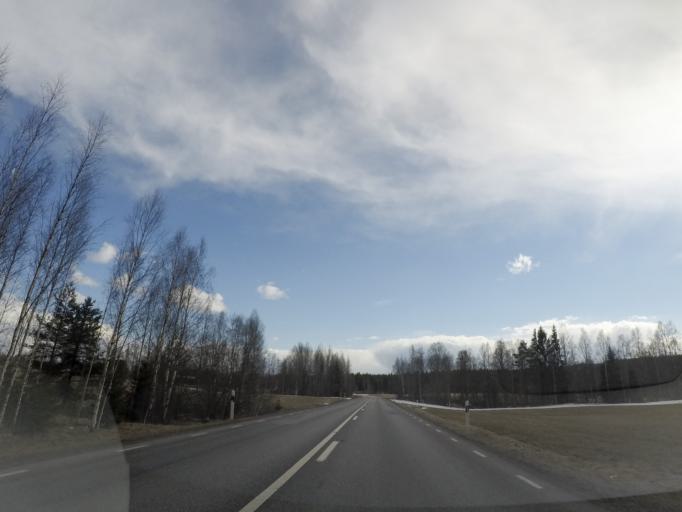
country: SE
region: Vaestmanland
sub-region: Skinnskattebergs Kommun
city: Skinnskatteberg
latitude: 59.8695
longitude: 15.6494
